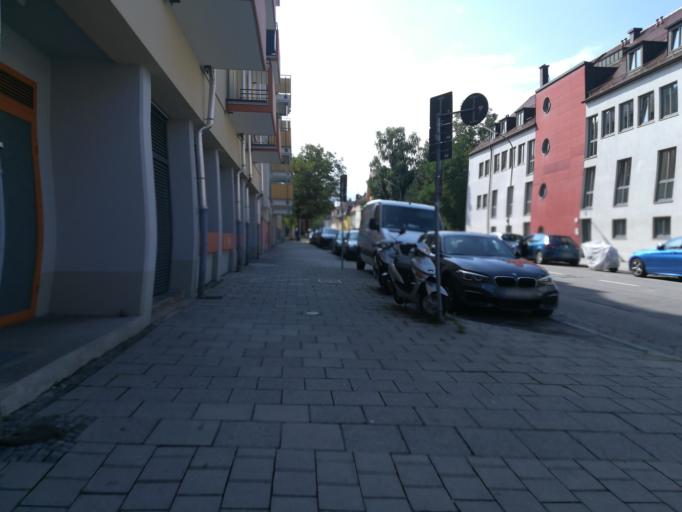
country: DE
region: Bavaria
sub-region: Upper Bavaria
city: Karlsfeld
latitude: 48.1816
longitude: 11.5214
